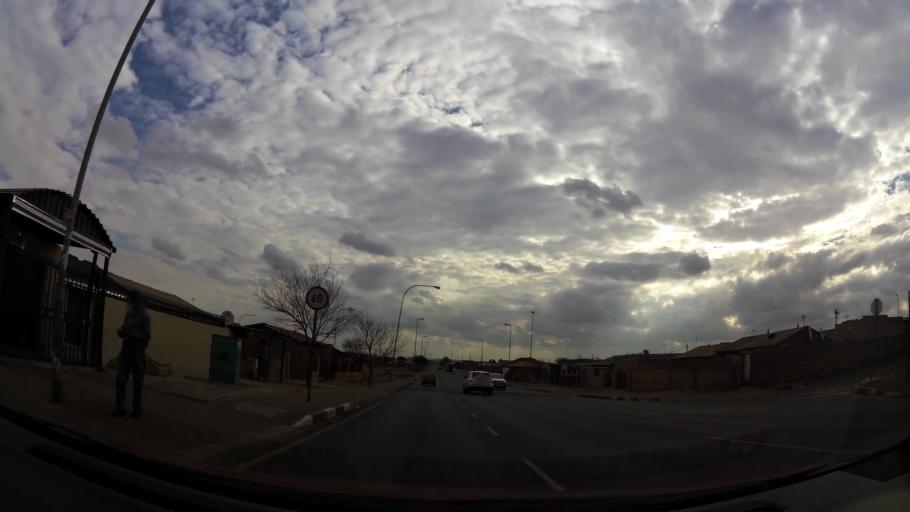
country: ZA
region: Gauteng
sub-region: City of Johannesburg Metropolitan Municipality
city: Soweto
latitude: -26.2488
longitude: 27.8214
